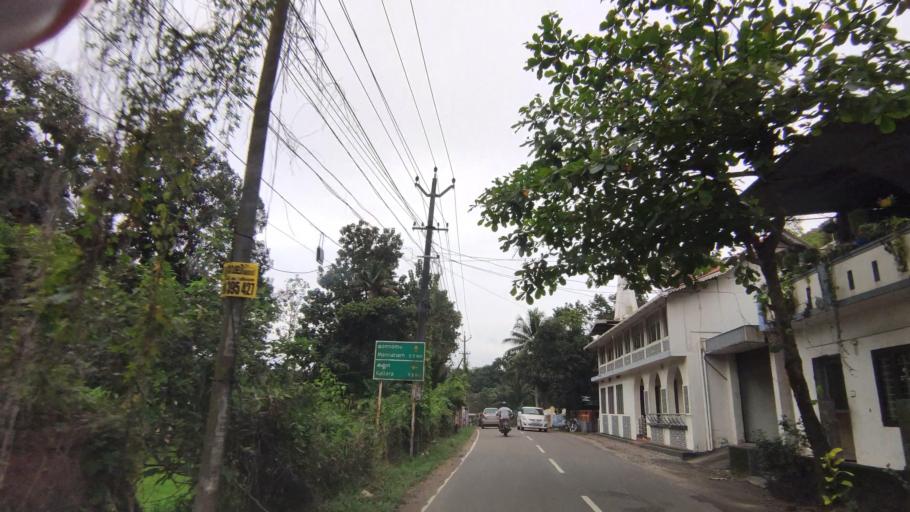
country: IN
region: Kerala
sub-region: Kottayam
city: Kottayam
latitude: 9.6454
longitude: 76.5182
